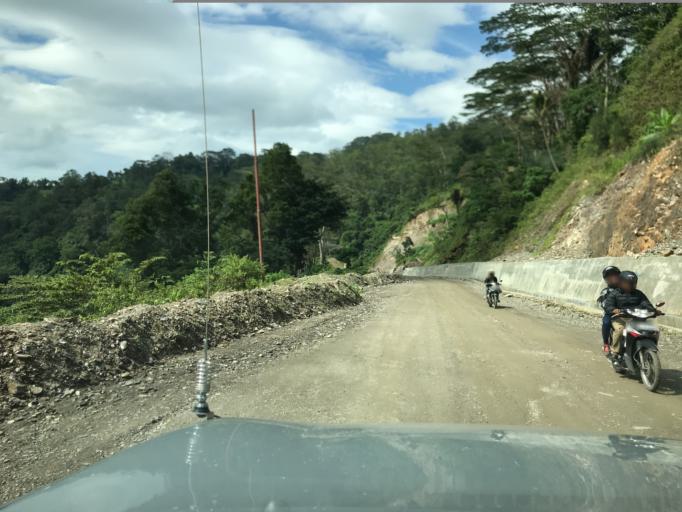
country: TL
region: Aileu
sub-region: Aileu Villa
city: Aileu
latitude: -8.6498
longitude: 125.5265
